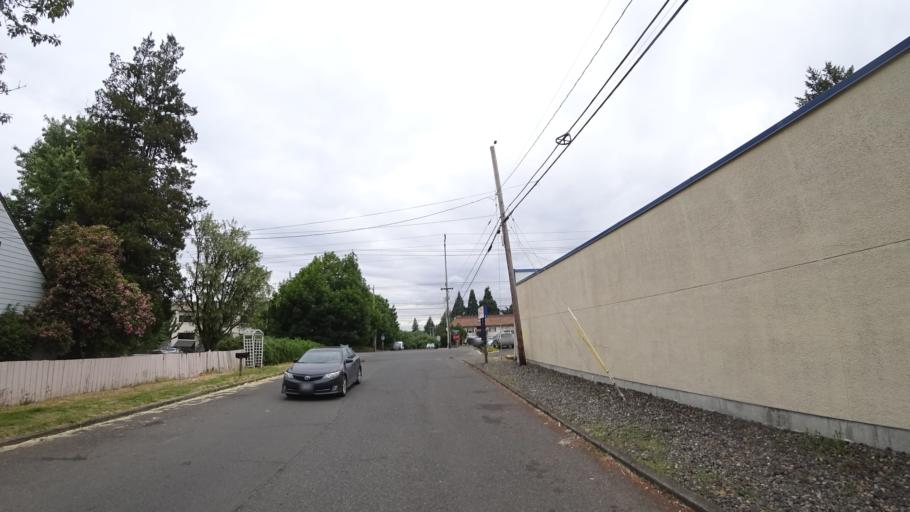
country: US
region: Oregon
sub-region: Multnomah County
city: Lents
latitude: 45.5038
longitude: -122.5596
